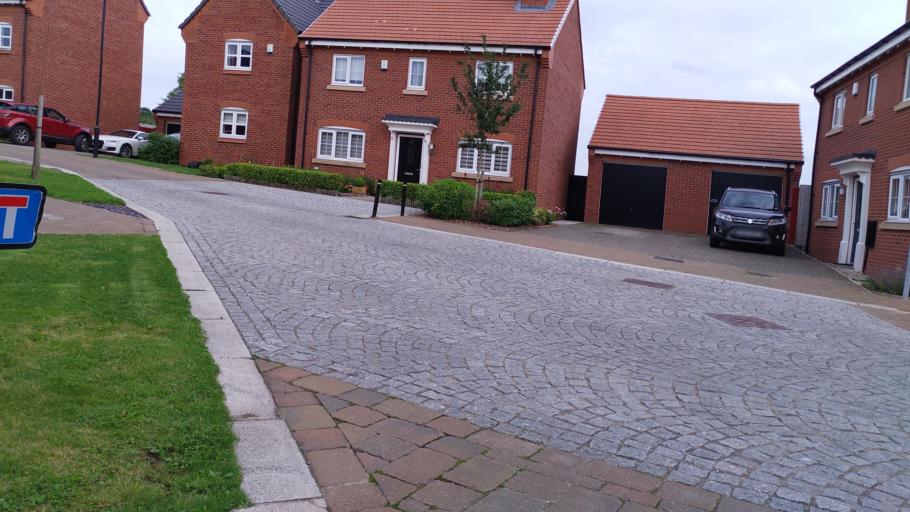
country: GB
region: England
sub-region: Lancashire
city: Coppull
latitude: 53.6295
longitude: -2.6363
